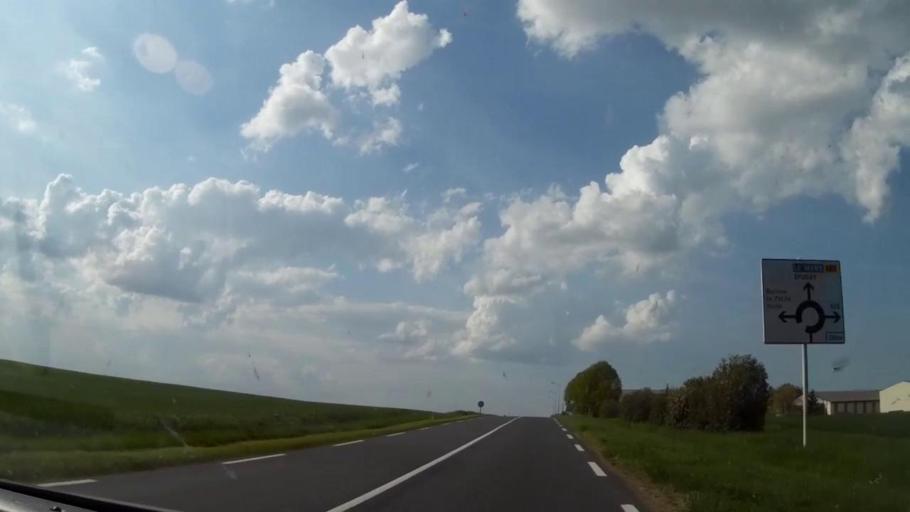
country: FR
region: Centre
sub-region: Departement du Loir-et-Cher
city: Aze
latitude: 47.8494
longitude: 0.9868
